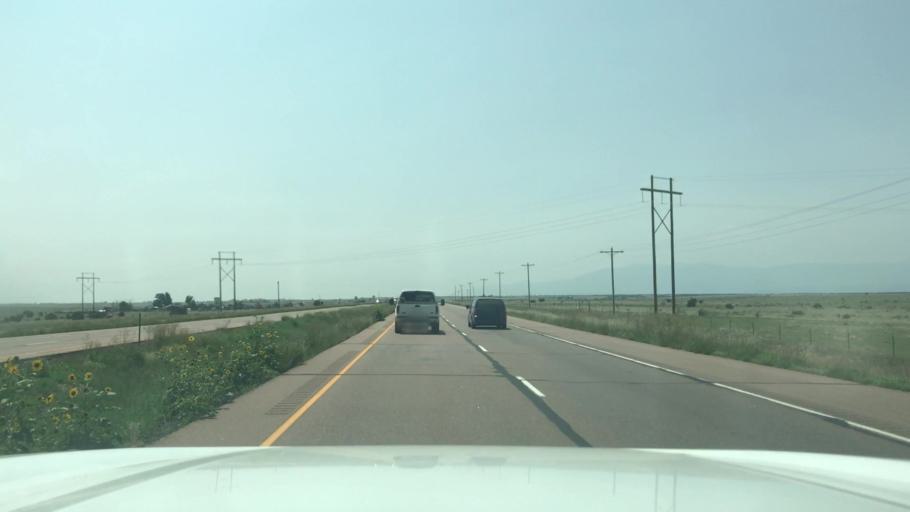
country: US
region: Colorado
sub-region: Pueblo County
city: Pueblo
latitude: 38.1021
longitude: -104.6845
